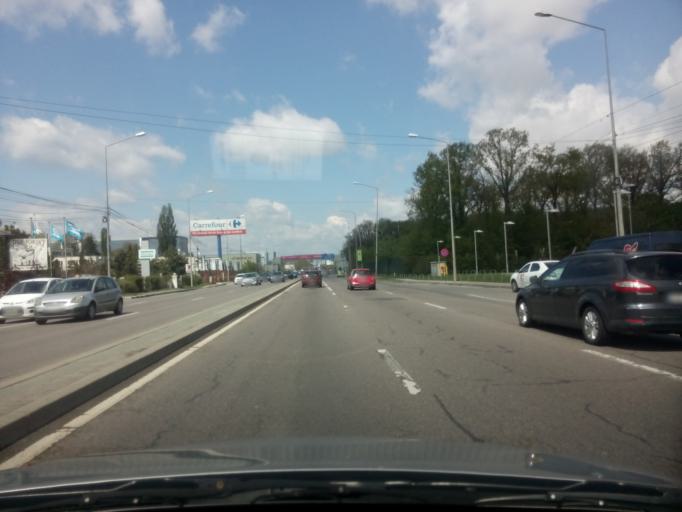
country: RO
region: Ilfov
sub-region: Comuna Otopeni
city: Otopeni
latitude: 44.5284
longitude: 26.0703
